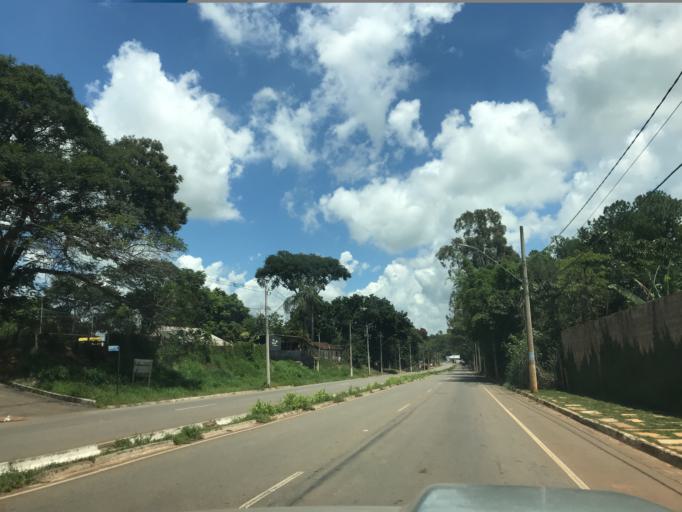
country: BR
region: Minas Gerais
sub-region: Tres Coracoes
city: Tres Coracoes
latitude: -21.6637
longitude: -45.2818
